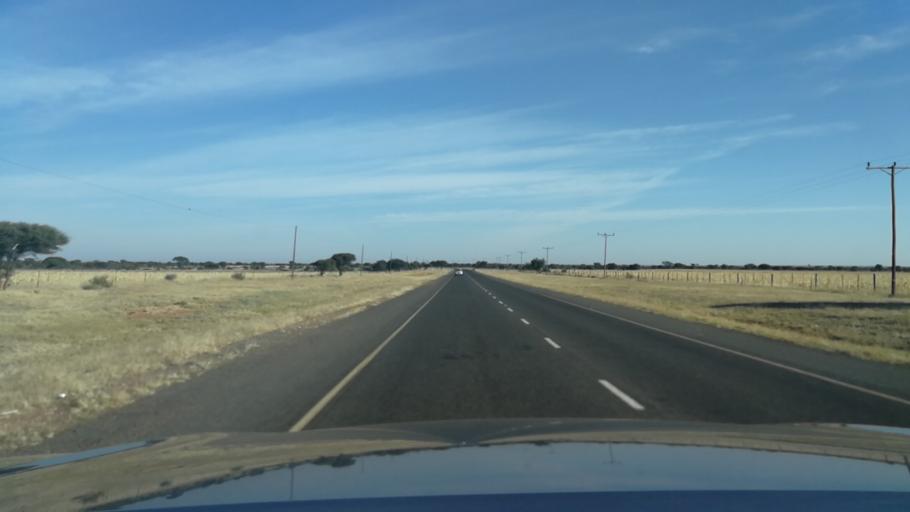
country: BW
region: South East
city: Janeng
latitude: -25.4772
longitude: 25.4988
